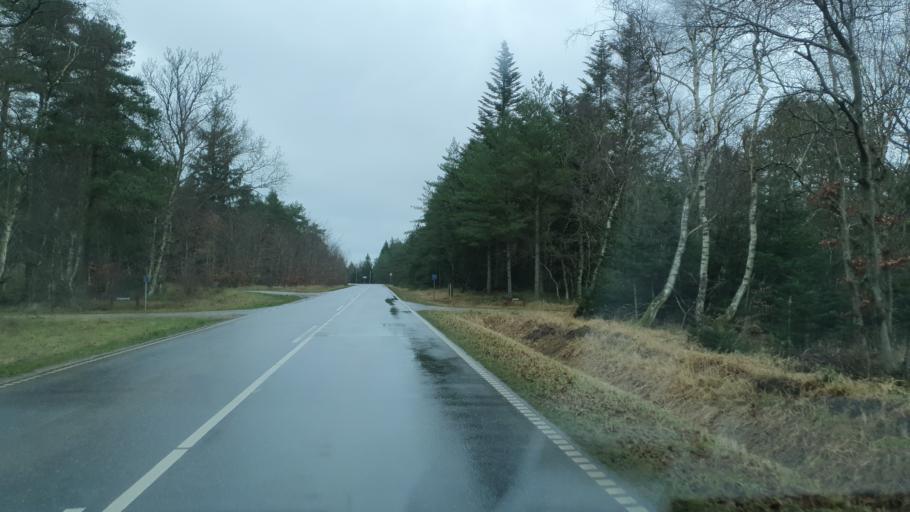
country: DK
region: North Denmark
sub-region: Jammerbugt Kommune
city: Fjerritslev
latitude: 57.1279
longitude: 9.1319
